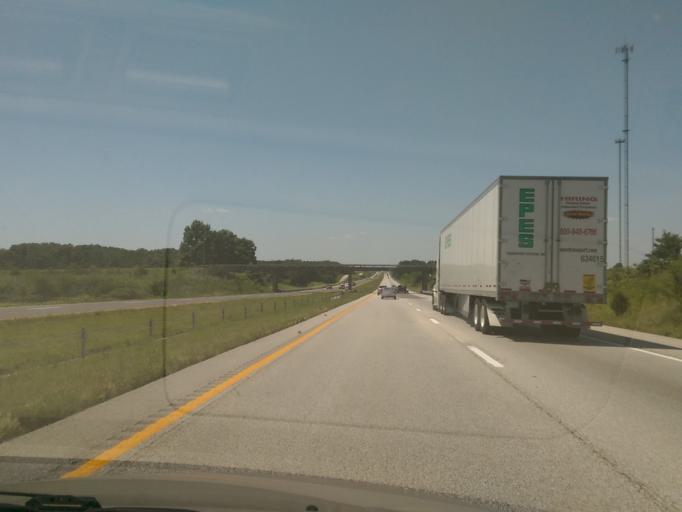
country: US
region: Missouri
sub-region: Saline County
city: Marshall
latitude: 38.9494
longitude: -93.0326
